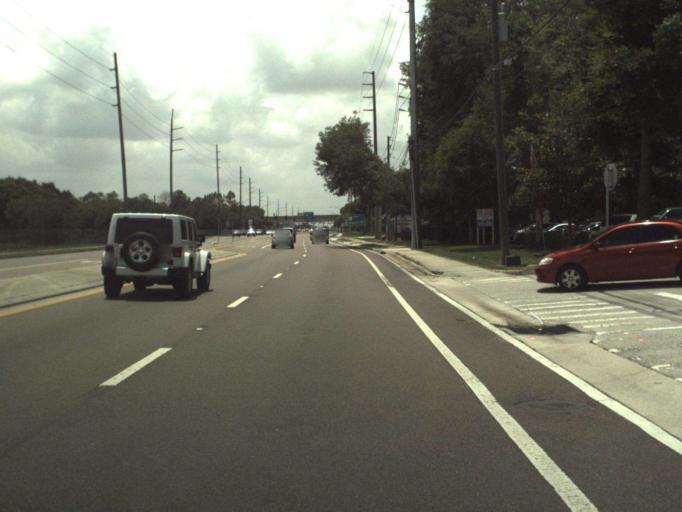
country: US
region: Florida
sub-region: Seminole County
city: Goldenrod
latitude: 28.6189
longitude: -81.2539
